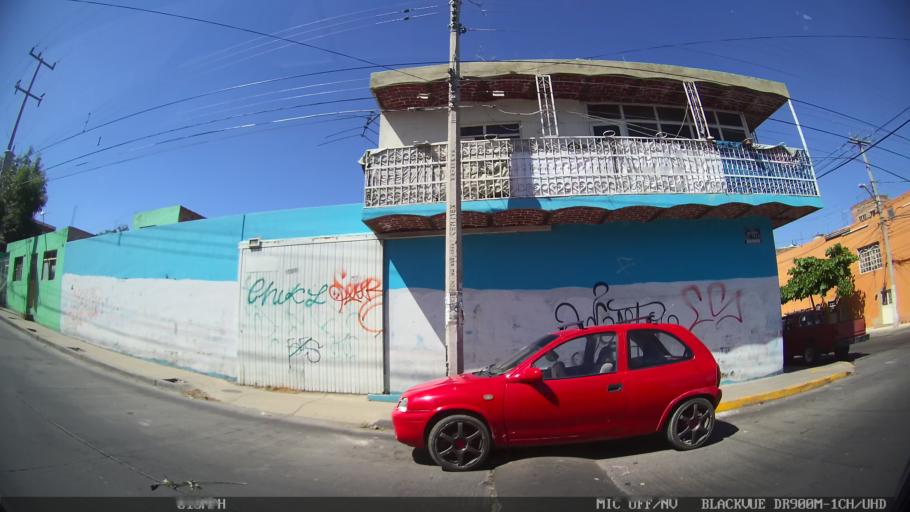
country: MX
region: Jalisco
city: Tlaquepaque
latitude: 20.6892
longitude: -103.2804
